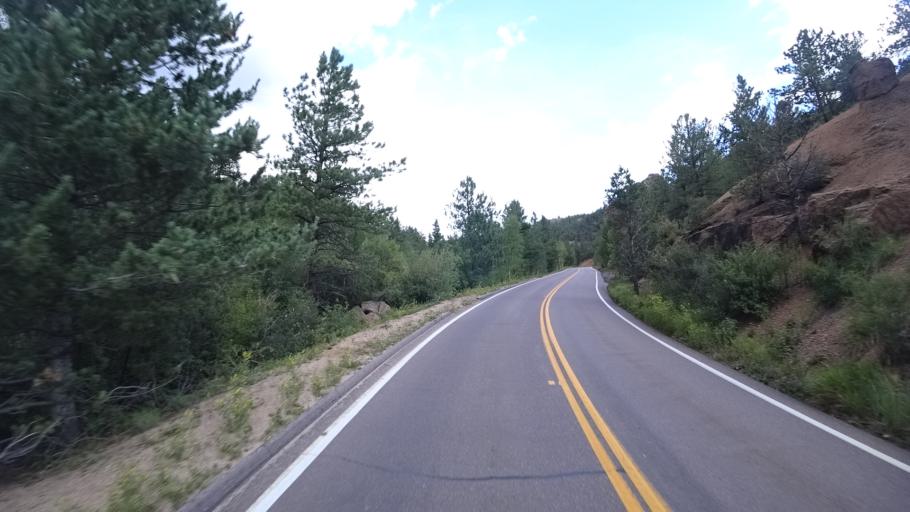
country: US
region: Colorado
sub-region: El Paso County
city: Cascade-Chipita Park
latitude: 38.9050
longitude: -105.0132
